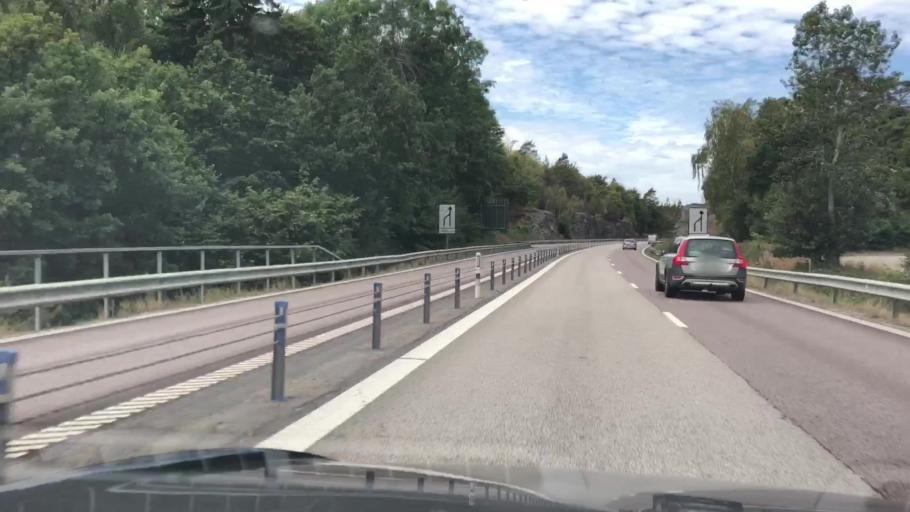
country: SE
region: Blekinge
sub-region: Karlskrona Kommun
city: Rodeby
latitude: 56.2061
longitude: 15.6319
